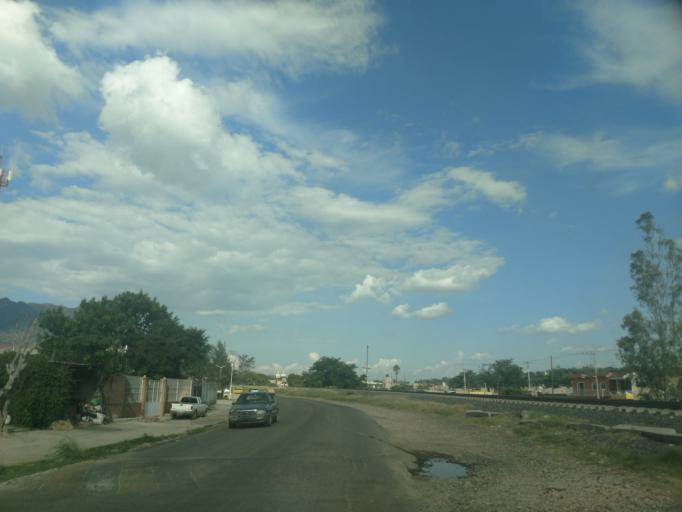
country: MX
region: Jalisco
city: Antonio Escobedo
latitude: 20.9051
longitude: -103.9827
